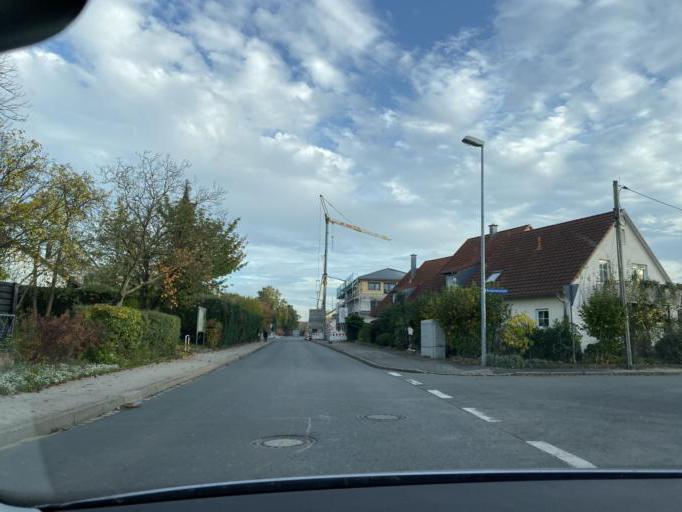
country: DE
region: Bavaria
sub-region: Regierungsbezirk Mittelfranken
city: Puschendorf
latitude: 49.5258
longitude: 10.8250
